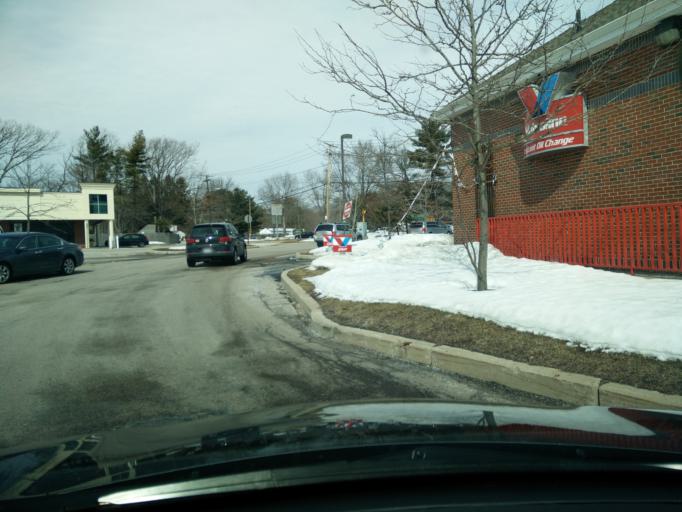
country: US
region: Massachusetts
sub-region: Norfolk County
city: Walpole
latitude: 42.1403
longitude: -71.2199
